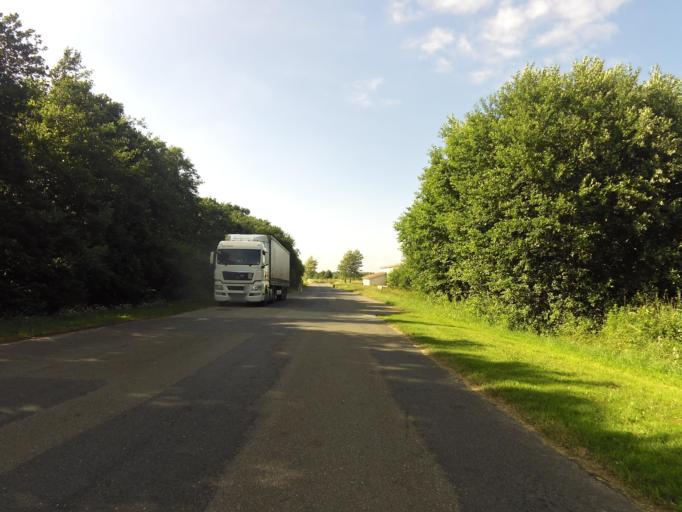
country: DK
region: South Denmark
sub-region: Vejen Kommune
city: Rodding
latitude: 55.3771
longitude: 9.0559
